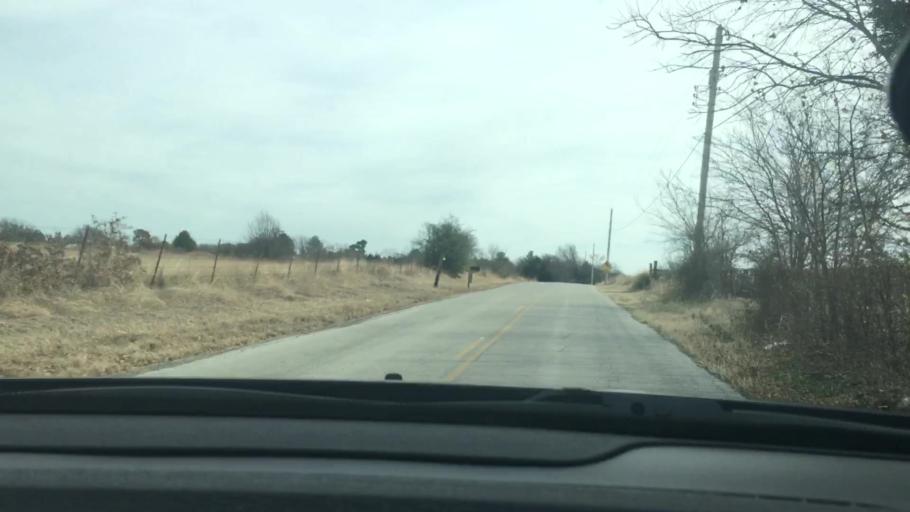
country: US
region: Oklahoma
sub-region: Carter County
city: Ardmore
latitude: 34.1737
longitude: -97.0813
